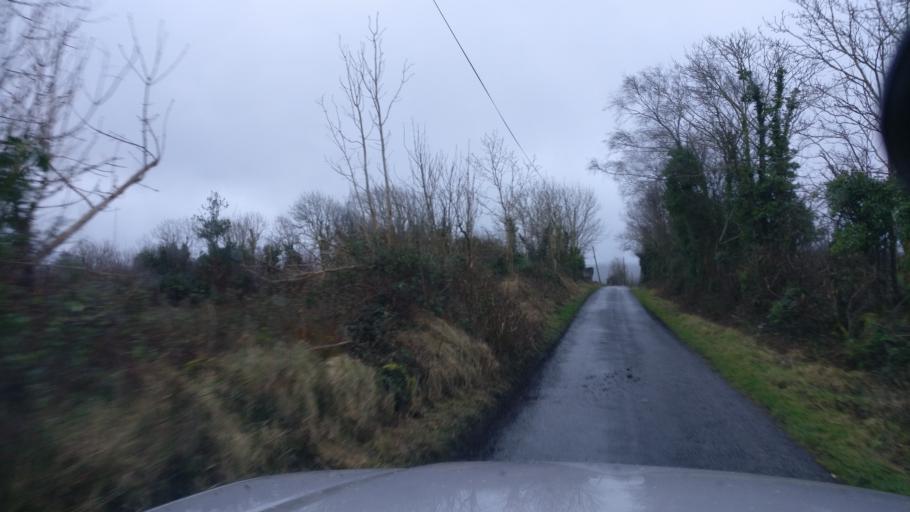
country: IE
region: Connaught
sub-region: County Galway
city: Loughrea
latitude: 53.1571
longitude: -8.6378
